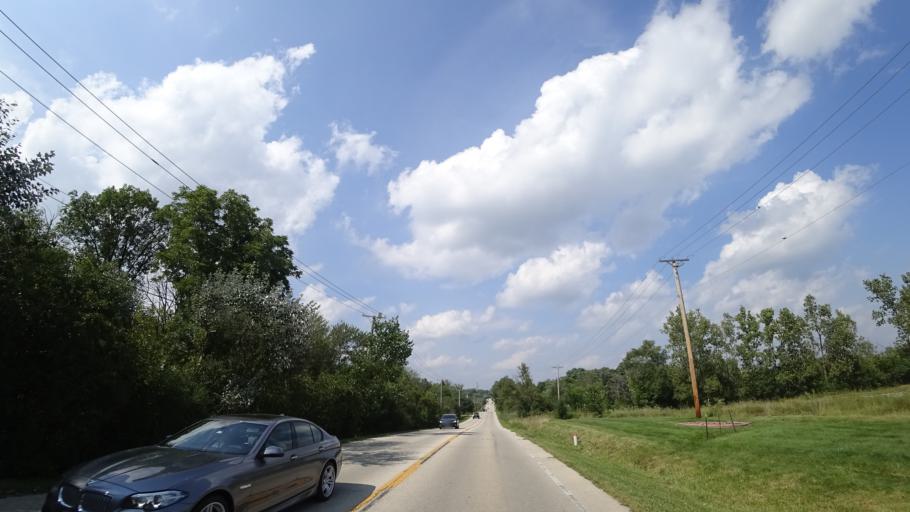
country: US
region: Illinois
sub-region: Cook County
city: Orland Park
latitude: 41.6457
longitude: -87.8926
